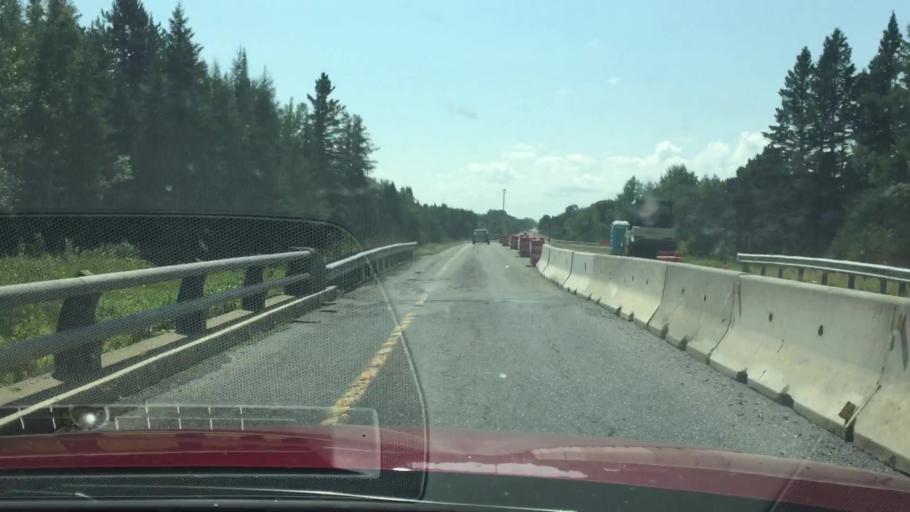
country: US
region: Maine
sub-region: Penobscot County
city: Patten
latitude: 45.8730
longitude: -68.4133
